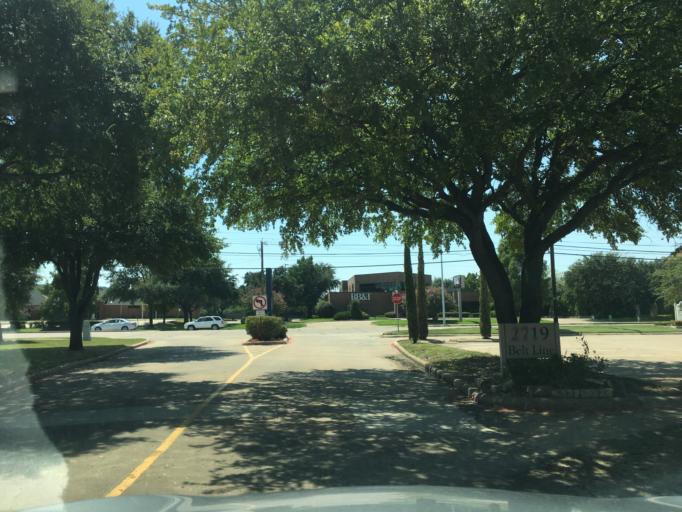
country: US
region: Texas
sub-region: Dallas County
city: Garland
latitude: 32.9455
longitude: -96.6693
